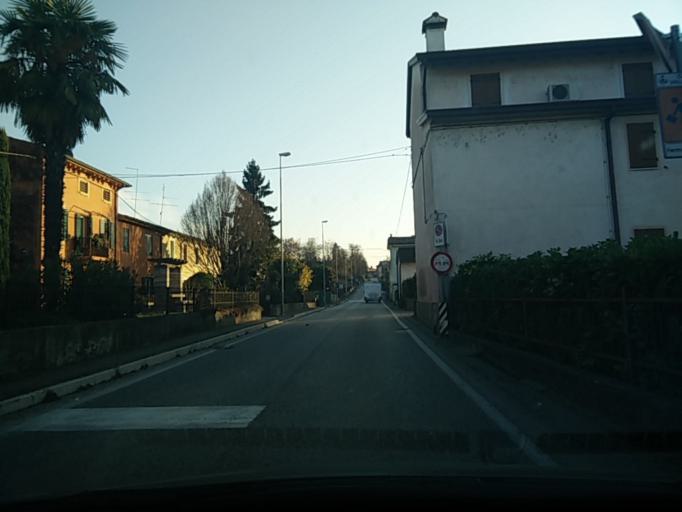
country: IT
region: Veneto
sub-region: Provincia di Verona
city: Salionze
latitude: 45.4077
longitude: 10.7201
